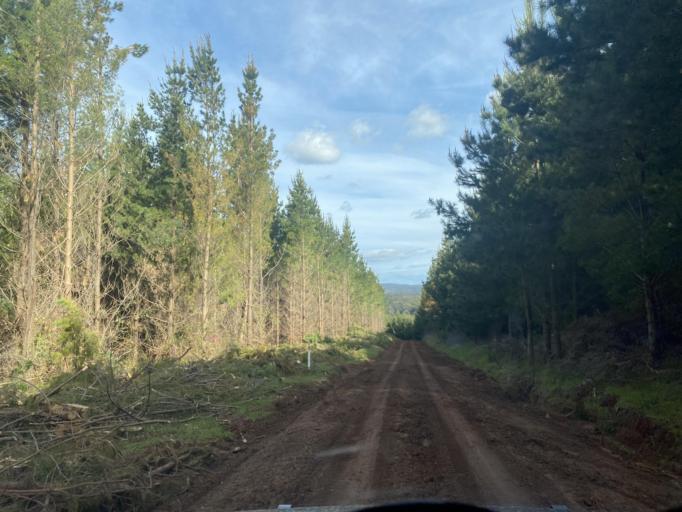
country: AU
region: Victoria
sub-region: Mansfield
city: Mansfield
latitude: -36.8363
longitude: 146.1785
